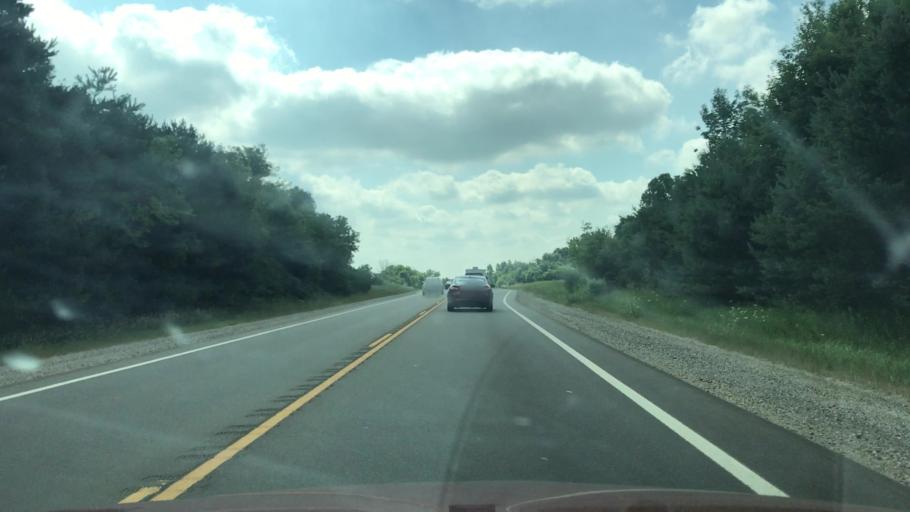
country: US
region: Michigan
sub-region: Kent County
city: Kent City
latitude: 43.2079
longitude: -85.7431
